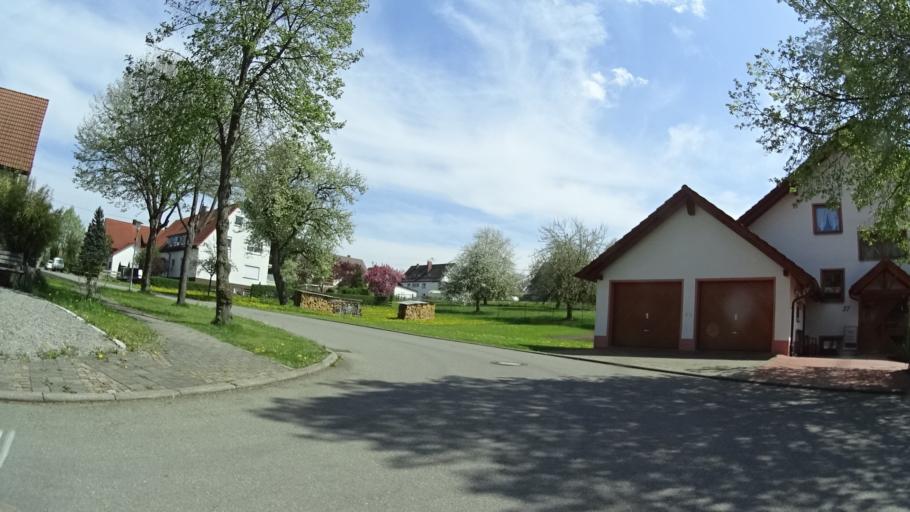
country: DE
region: Baden-Wuerttemberg
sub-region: Freiburg Region
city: Dietingen
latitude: 48.2044
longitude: 8.6437
